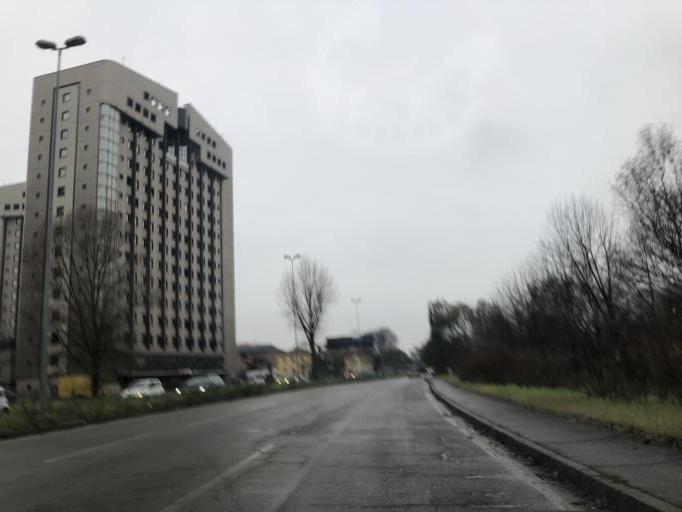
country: IT
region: Emilia-Romagna
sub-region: Provincia di Modena
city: Modena
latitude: 44.6354
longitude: 10.8976
